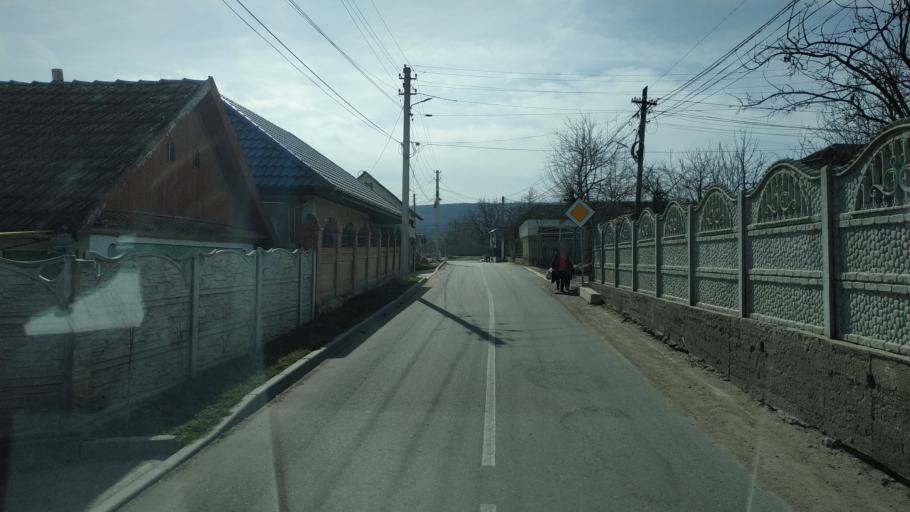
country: MD
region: Straseni
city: Straseni
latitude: 47.0946
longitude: 28.6515
